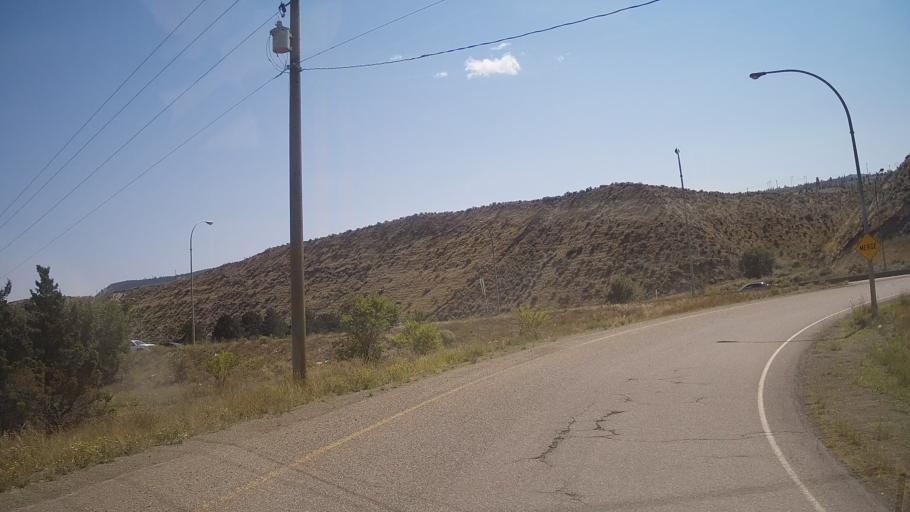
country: CA
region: British Columbia
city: Kamloops
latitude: 50.6729
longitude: -120.3007
